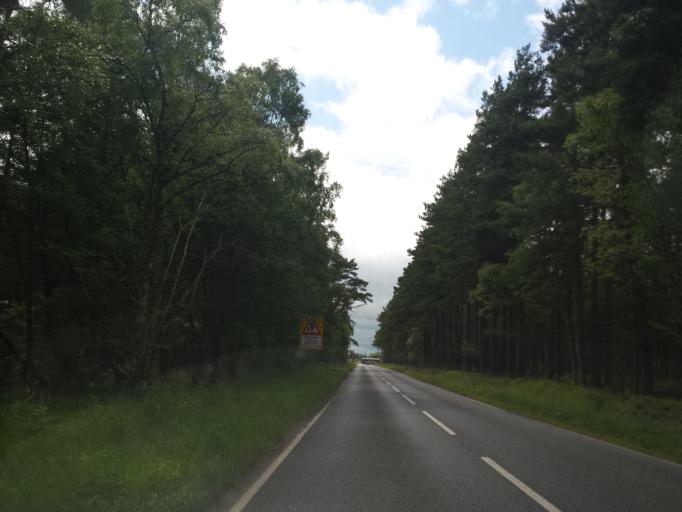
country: GB
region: Scotland
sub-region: Highland
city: Fortrose
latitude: 57.4813
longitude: -4.0838
